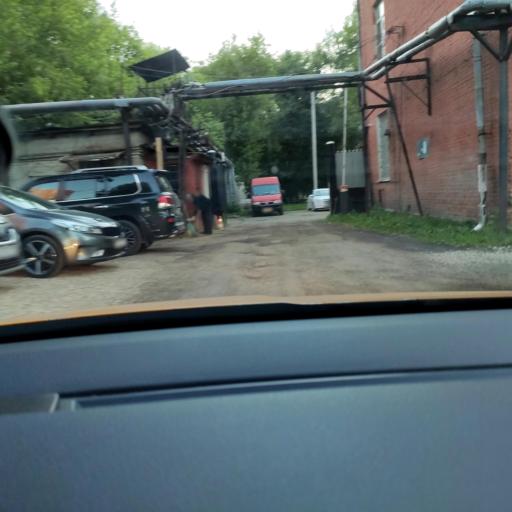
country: RU
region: Moskovskaya
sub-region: Podol'skiy Rayon
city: Podol'sk
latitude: 55.4290
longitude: 37.5212
